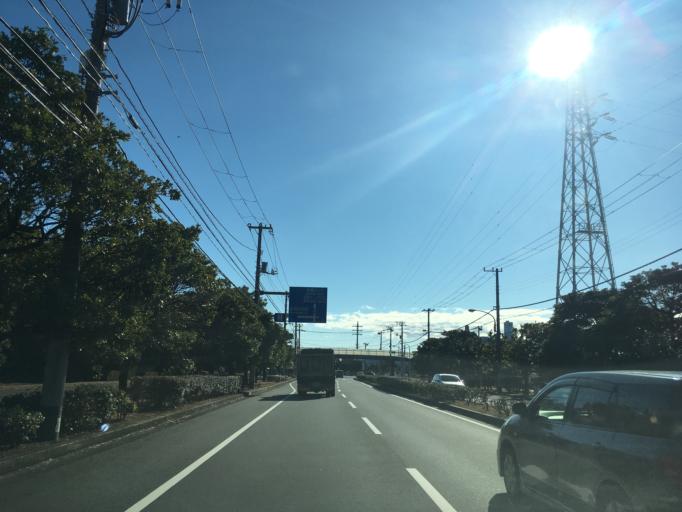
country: JP
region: Chiba
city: Funabashi
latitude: 35.6634
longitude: 140.0103
